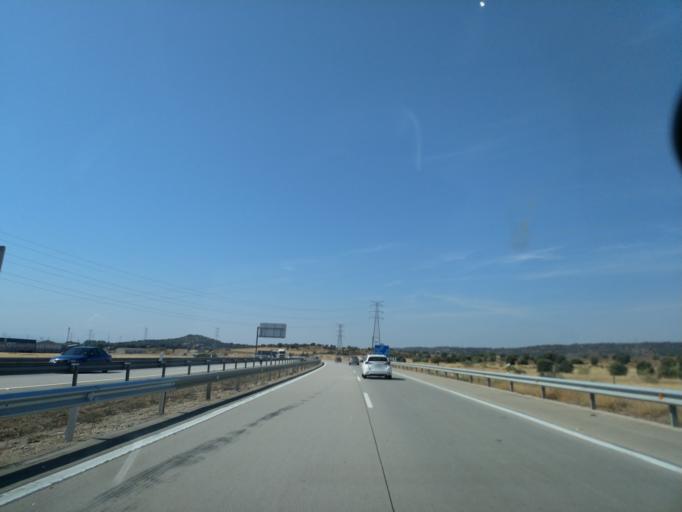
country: ES
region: Castille-La Mancha
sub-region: Province of Toledo
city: Talavera de la Reina
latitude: 40.0054
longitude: -4.8253
